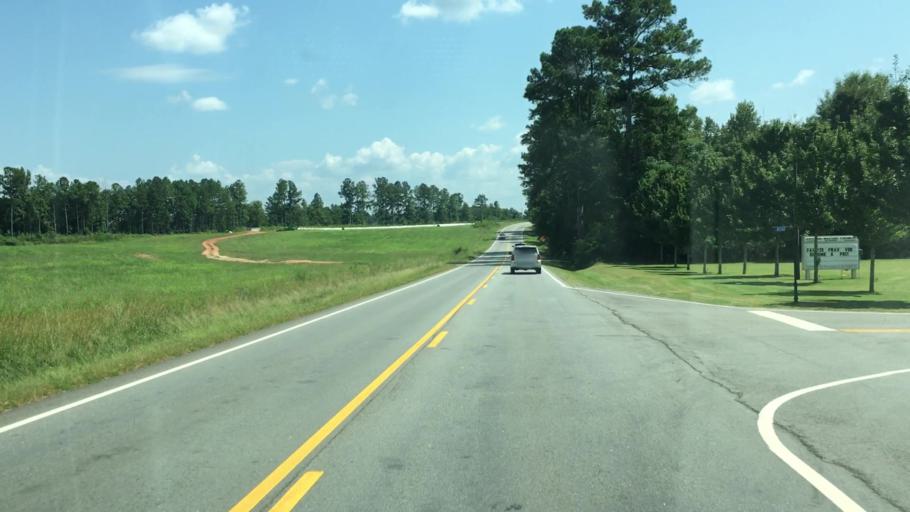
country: US
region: Georgia
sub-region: Oconee County
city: Watkinsville
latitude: 33.8097
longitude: -83.4305
